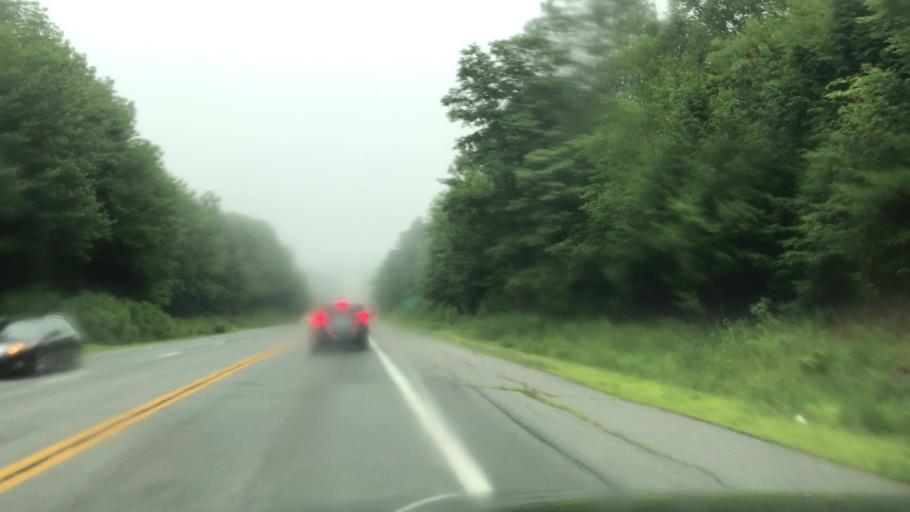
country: US
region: Maine
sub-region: Lincoln County
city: Waldoboro
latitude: 44.1000
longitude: -69.3958
